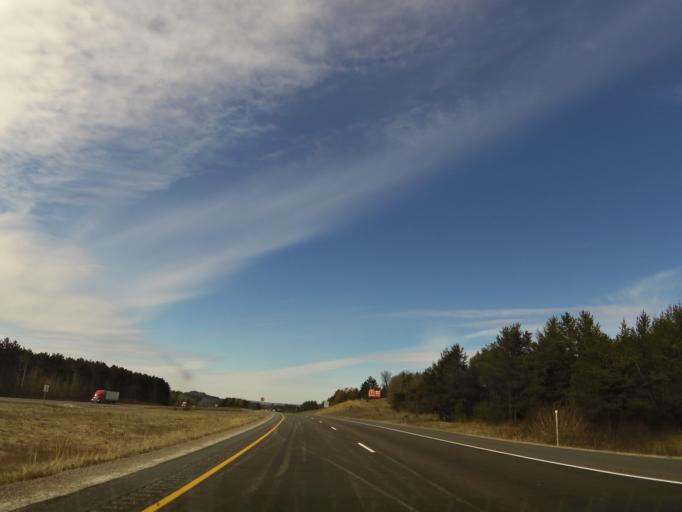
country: US
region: Wisconsin
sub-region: Trempealeau County
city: Osseo
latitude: 44.5140
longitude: -91.1369
